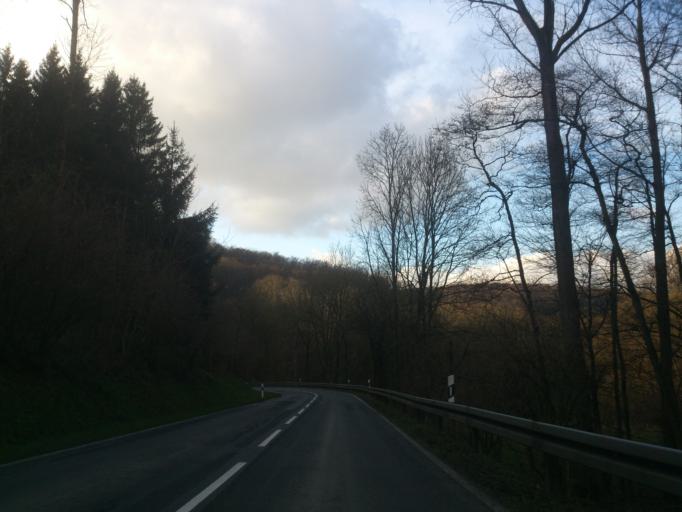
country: DE
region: Lower Saxony
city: Boffzen
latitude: 51.7502
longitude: 9.2927
